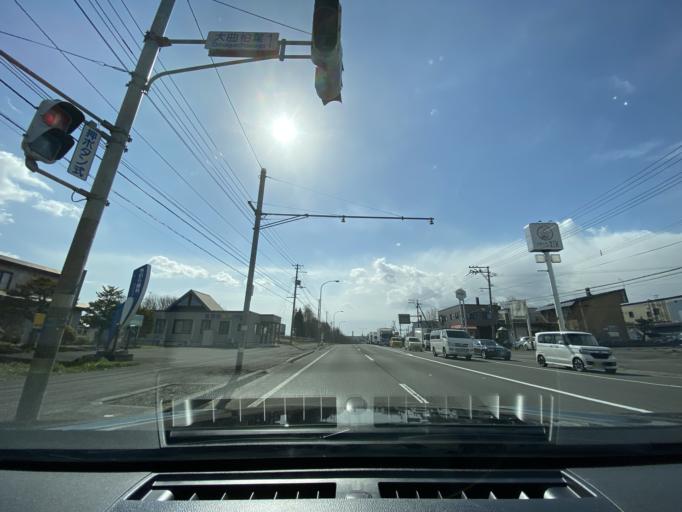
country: JP
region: Hokkaido
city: Kitahiroshima
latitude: 42.9704
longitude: 141.4796
